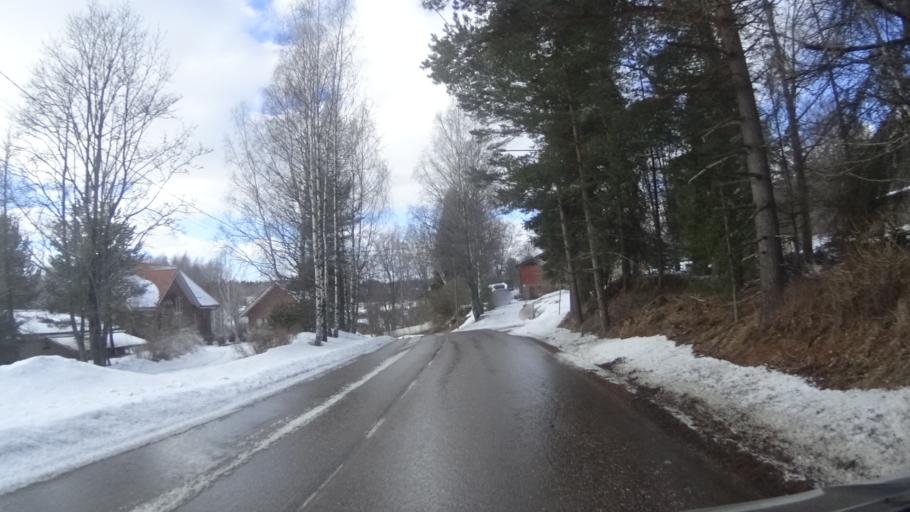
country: FI
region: Uusimaa
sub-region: Helsinki
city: Vantaa
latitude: 60.2552
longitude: 25.1593
